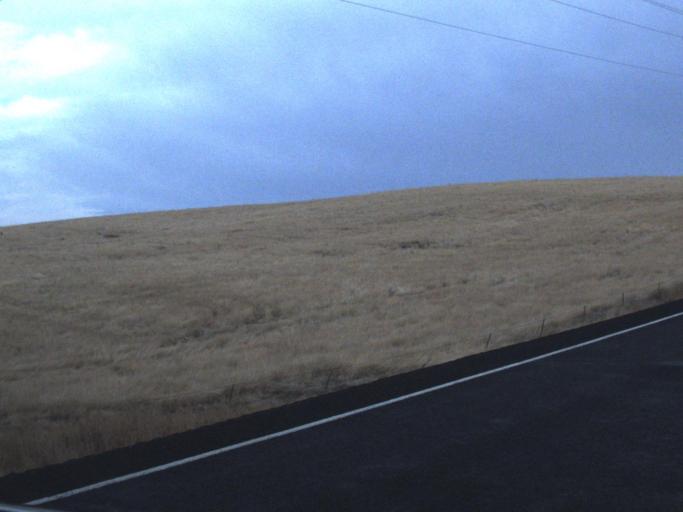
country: US
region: Washington
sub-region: Lincoln County
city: Davenport
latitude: 47.8124
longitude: -118.1803
